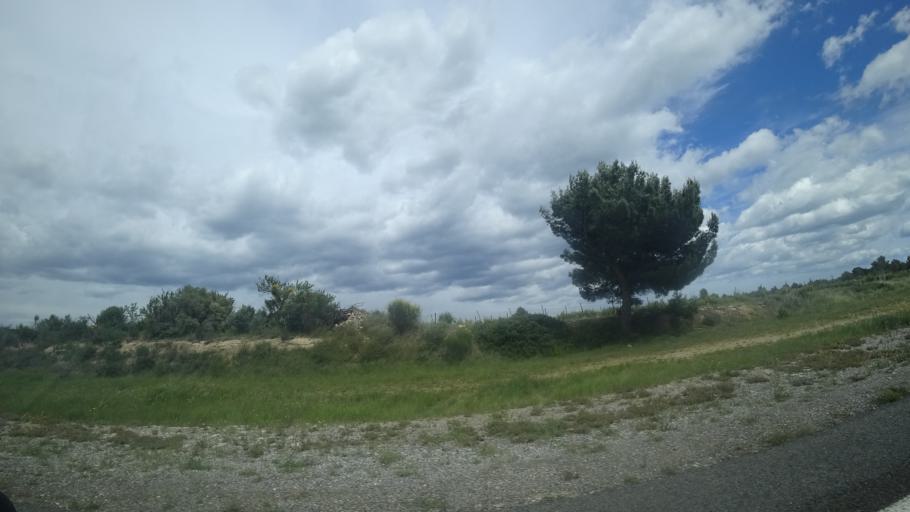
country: FR
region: Languedoc-Roussillon
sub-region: Departement de l'Aude
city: Leucate
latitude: 42.9268
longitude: 3.0186
